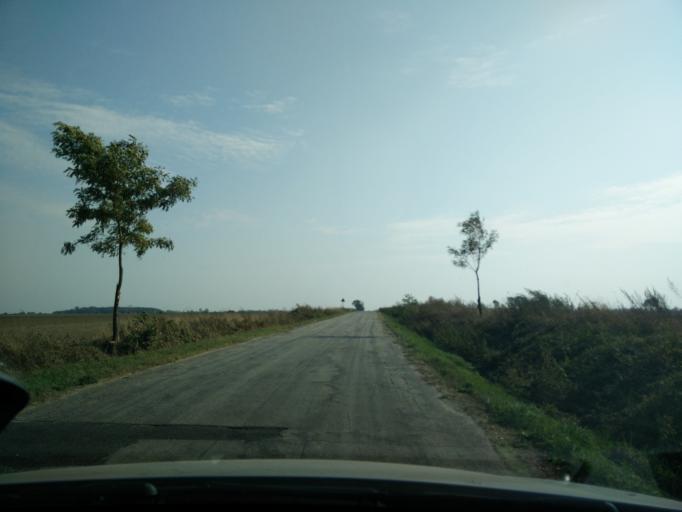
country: PL
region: Greater Poland Voivodeship
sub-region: Powiat sredzki
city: Dominowo
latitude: 52.2856
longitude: 17.3167
